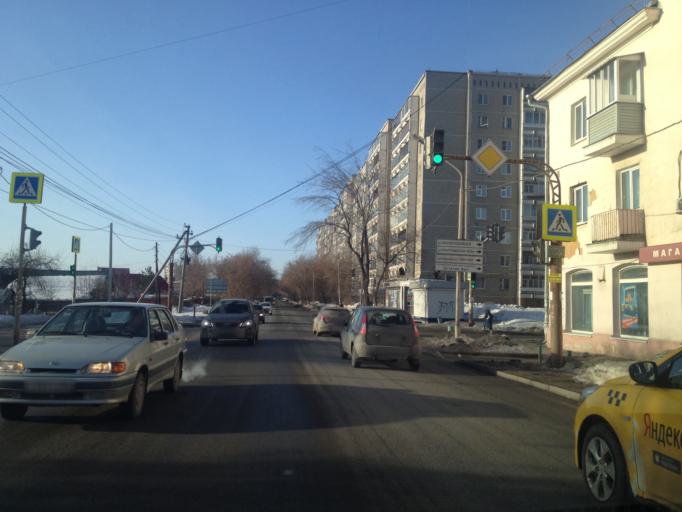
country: RU
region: Sverdlovsk
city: Sovkhoznyy
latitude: 56.7538
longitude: 60.6234
